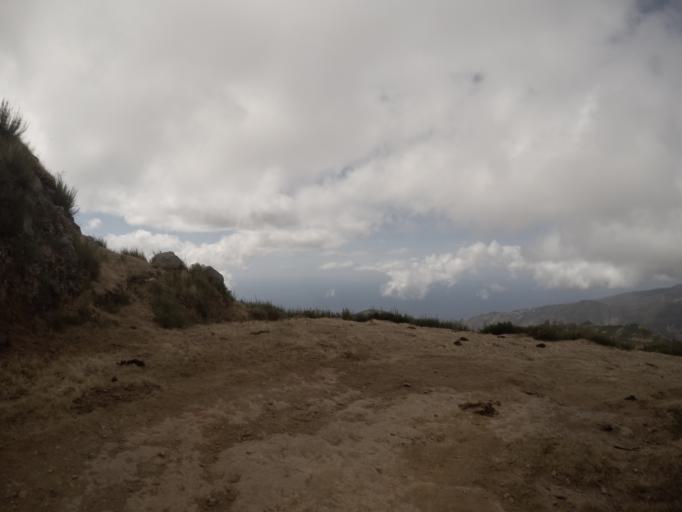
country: PT
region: Madeira
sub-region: Camara de Lobos
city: Curral das Freiras
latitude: 32.7138
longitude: -17.0076
